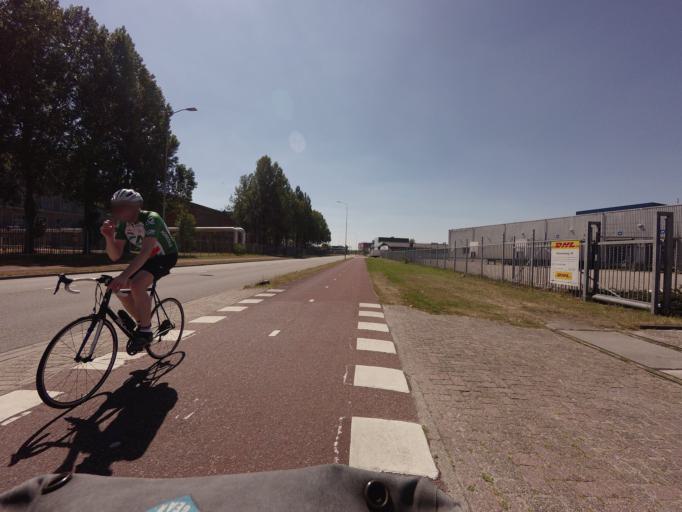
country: NL
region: Utrecht
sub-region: Stichtse Vecht
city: Maarssen
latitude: 52.1035
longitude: 5.0681
